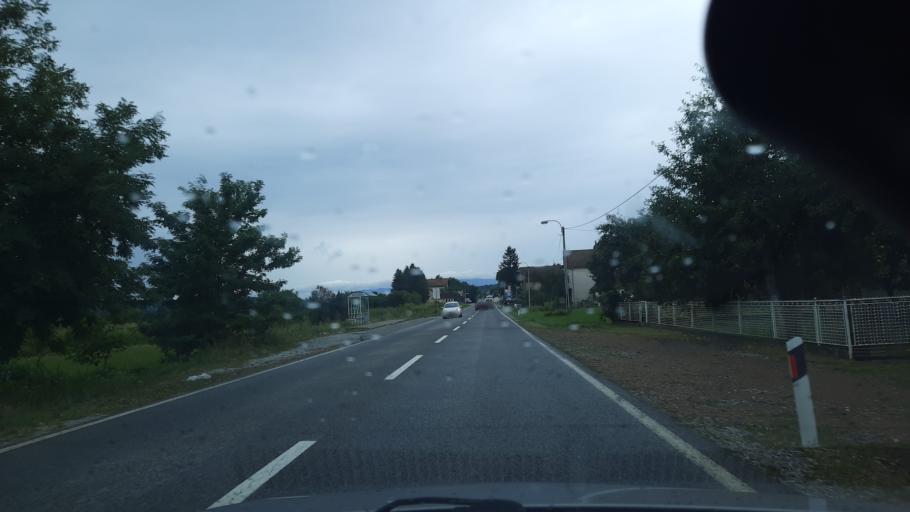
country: RS
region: Central Serbia
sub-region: Raski Okrug
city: Kraljevo
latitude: 43.7941
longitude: 20.7892
